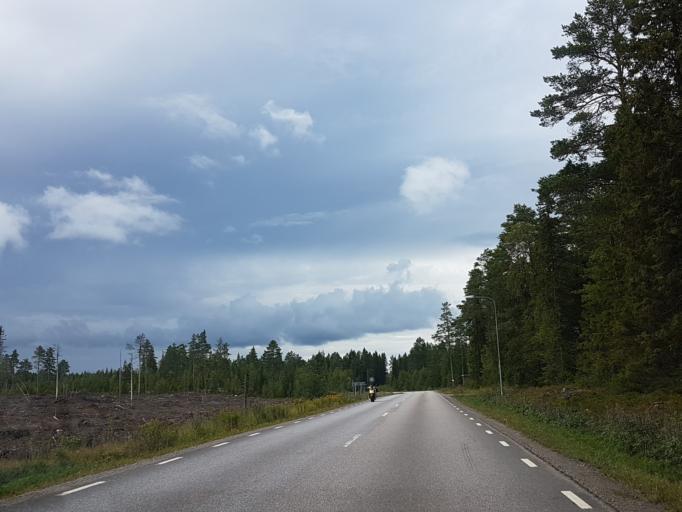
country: SE
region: Vaesterbotten
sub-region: Umea Kommun
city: Holmsund
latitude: 63.7862
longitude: 20.3847
